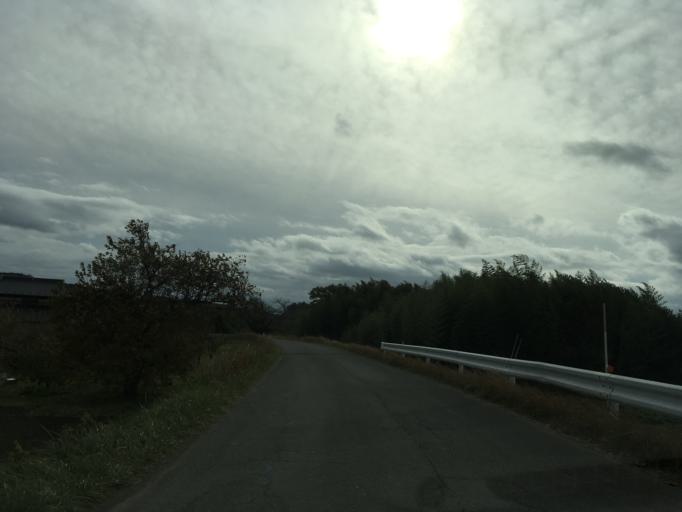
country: JP
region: Iwate
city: Ichinoseki
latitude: 38.7606
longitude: 141.2764
